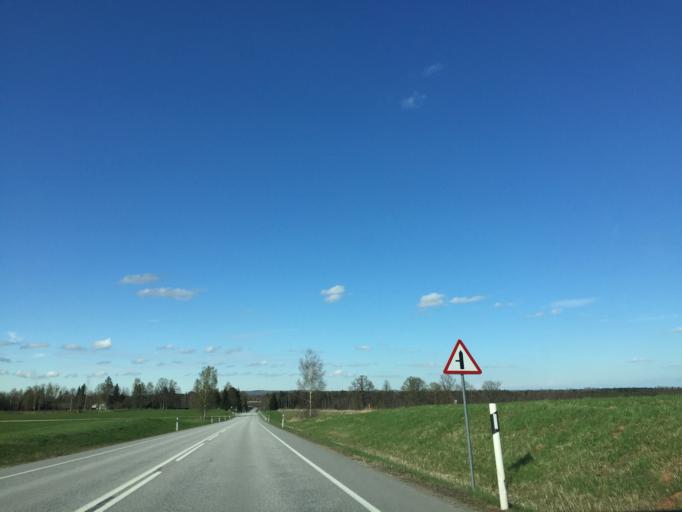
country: EE
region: Vorumaa
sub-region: Antsla vald
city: Vana-Antsla
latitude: 57.8815
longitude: 26.2816
